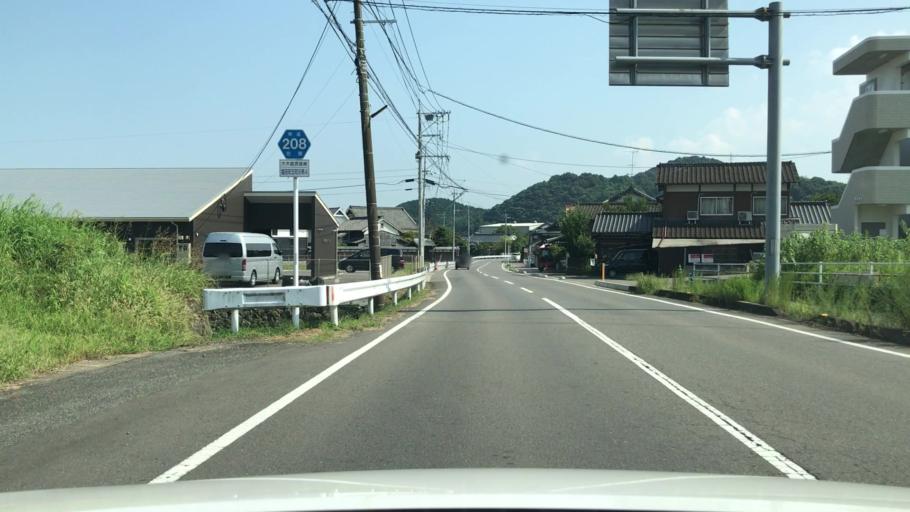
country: JP
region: Saga Prefecture
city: Kashima
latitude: 33.1251
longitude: 130.0624
